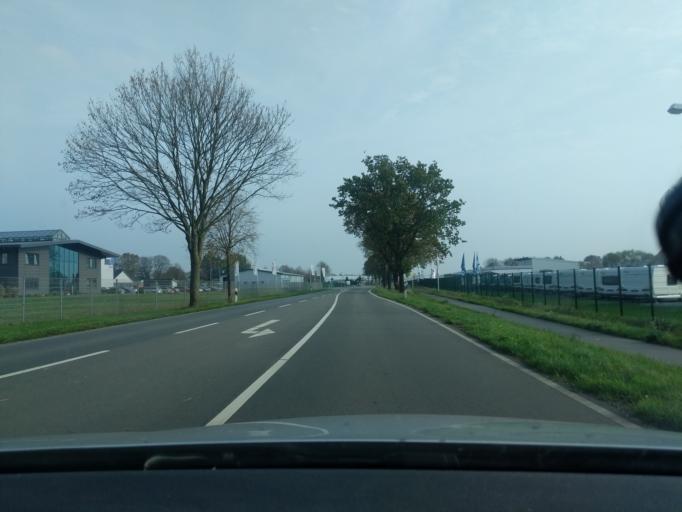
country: DE
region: Lower Saxony
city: Lamstedt
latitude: 53.6385
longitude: 9.0816
